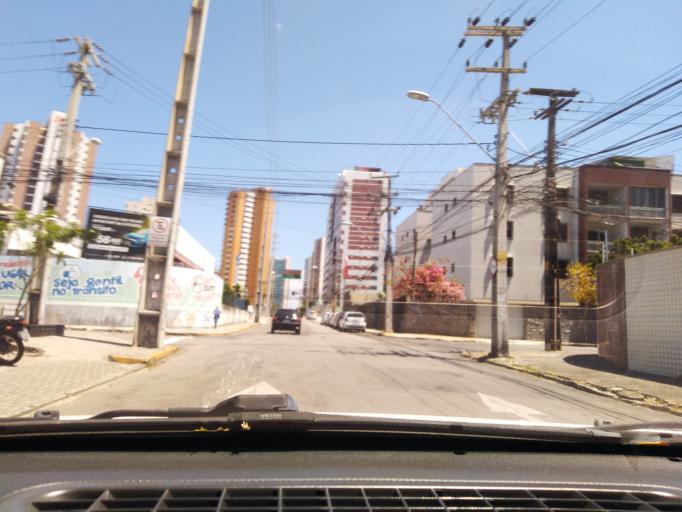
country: BR
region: Ceara
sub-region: Fortaleza
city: Fortaleza
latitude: -3.7426
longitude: -38.4749
